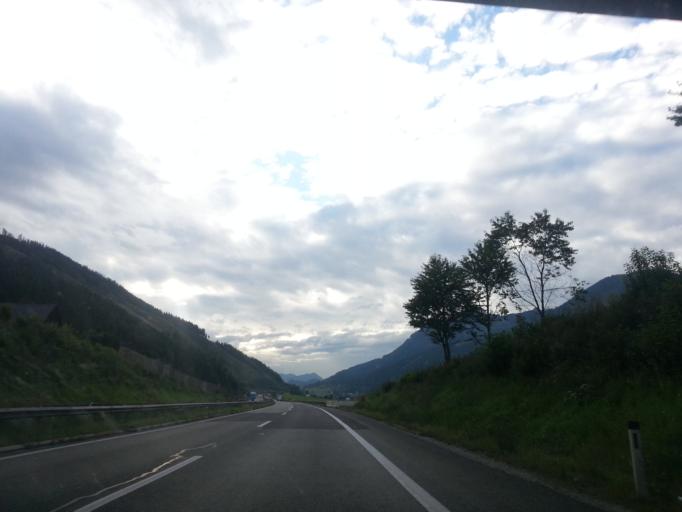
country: AT
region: Styria
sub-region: Politischer Bezirk Leoben
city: Kammern im Liesingtal
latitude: 47.3824
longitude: 14.9383
